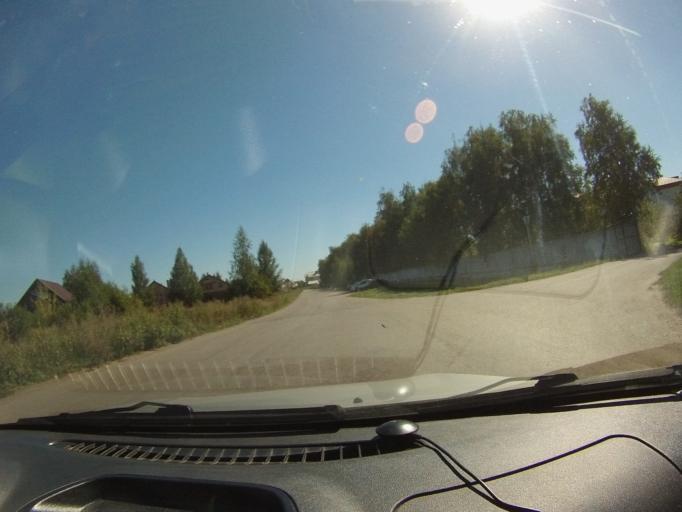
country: RU
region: Tambov
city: Komsomolets
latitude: 52.7679
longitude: 41.3617
